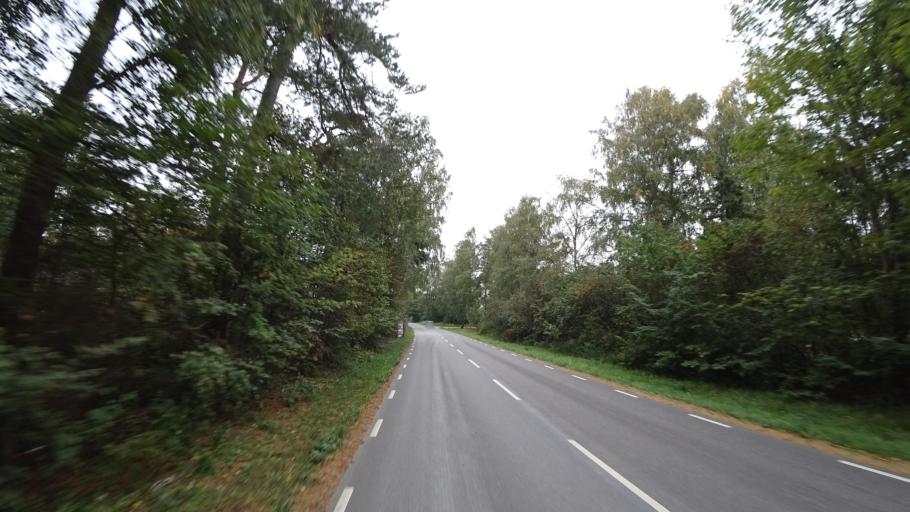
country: SE
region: Skane
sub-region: Kavlinge Kommun
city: Hofterup
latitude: 55.8161
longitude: 12.9746
